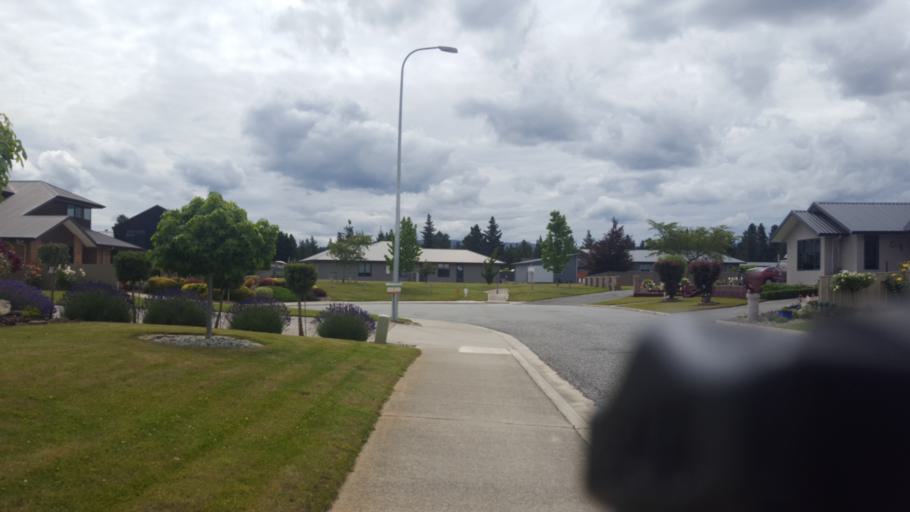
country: NZ
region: Otago
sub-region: Queenstown-Lakes District
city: Wanaka
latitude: -45.2445
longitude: 169.3753
